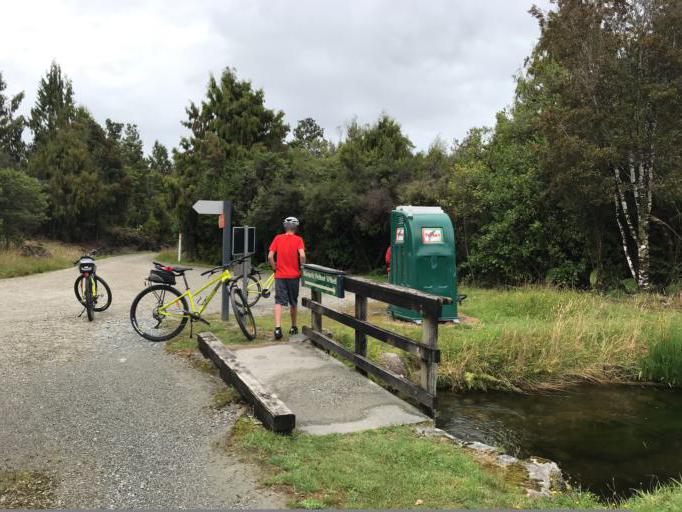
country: NZ
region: West Coast
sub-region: Westland District
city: Hokitika
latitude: -42.7814
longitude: 171.1279
